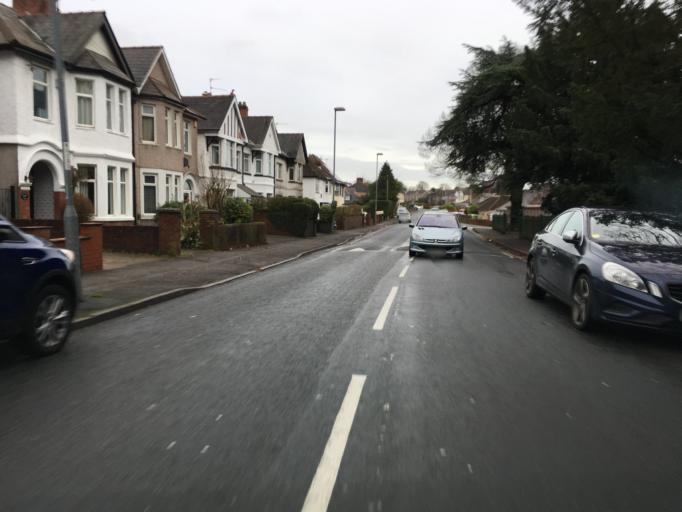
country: GB
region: Wales
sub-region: Newport
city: Caerleon
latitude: 51.5943
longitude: -2.9628
